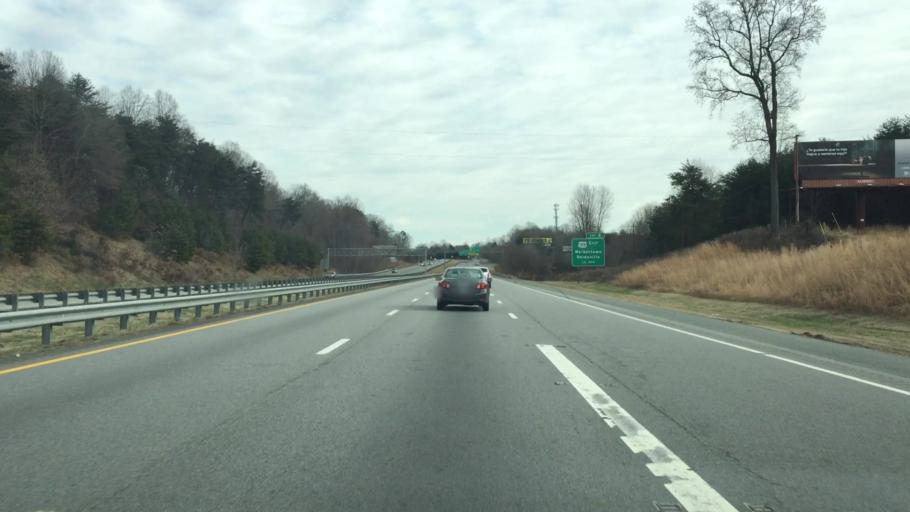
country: US
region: North Carolina
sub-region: Forsyth County
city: Winston-Salem
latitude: 36.0990
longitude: -80.2034
